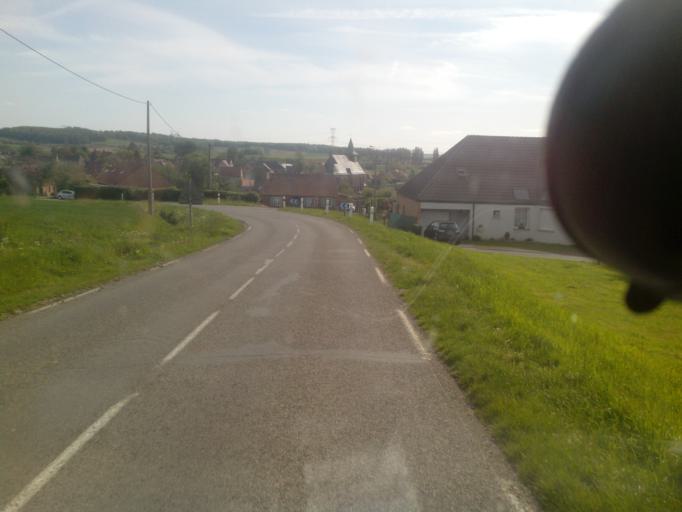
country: FR
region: Nord-Pas-de-Calais
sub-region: Departement du Nord
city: Renescure
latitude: 50.7354
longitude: 2.4116
